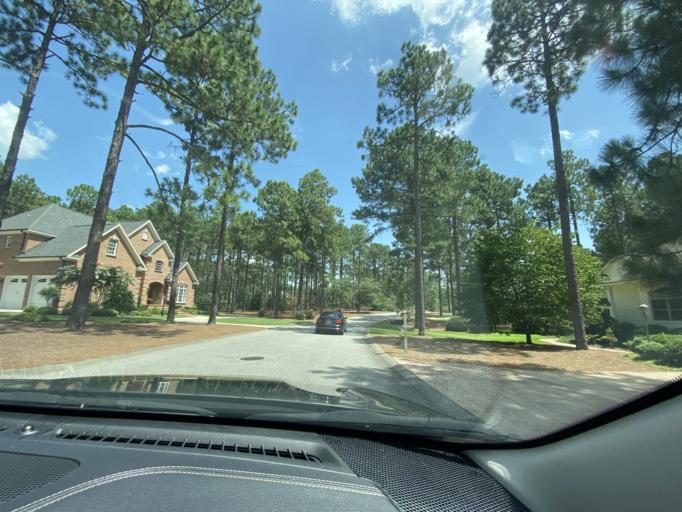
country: US
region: North Carolina
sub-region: Moore County
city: Pinehurst
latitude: 35.1969
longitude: -79.4293
